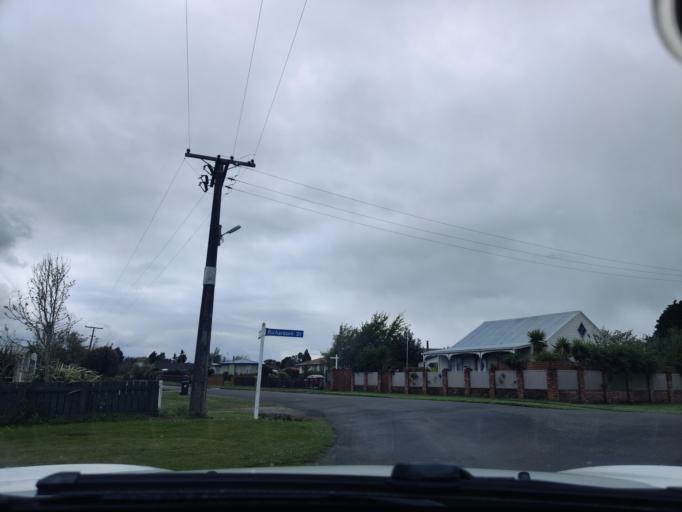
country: NZ
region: Manawatu-Wanganui
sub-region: Palmerston North City
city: Palmerston North
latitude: -40.3345
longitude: 175.8647
